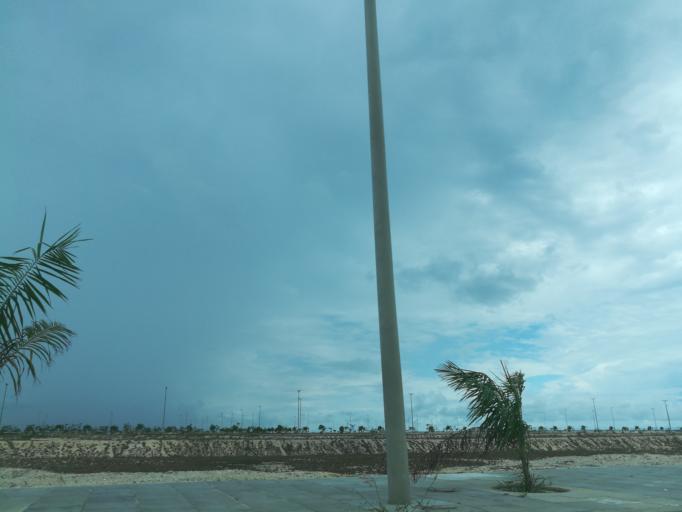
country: NG
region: Lagos
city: Ikoyi
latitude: 6.4067
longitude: 3.4151
